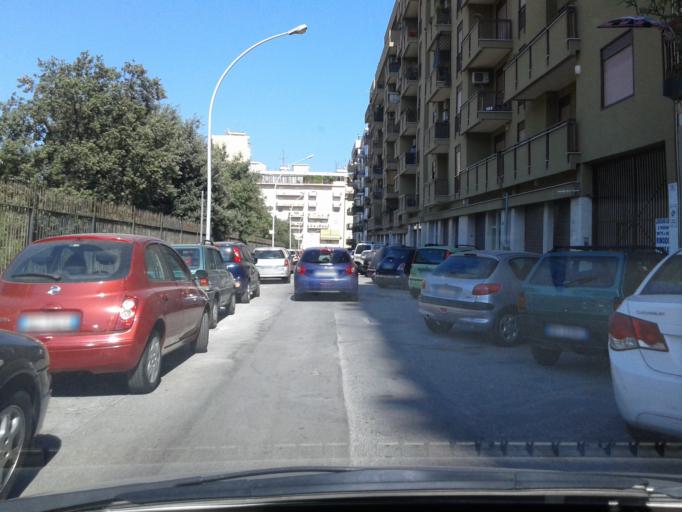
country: IT
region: Sicily
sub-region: Palermo
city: Palermo
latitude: 38.1059
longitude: 13.3354
